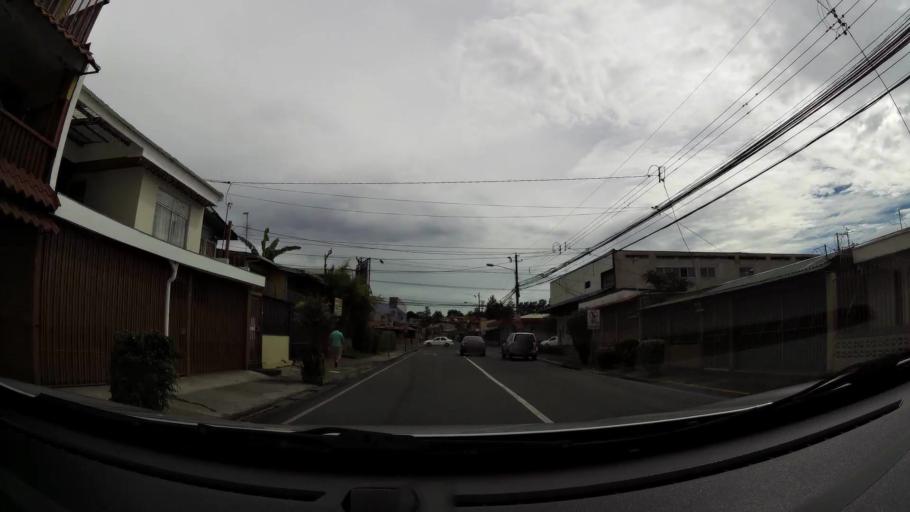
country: CR
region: San Jose
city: Curridabat
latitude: 9.9123
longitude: -84.0366
